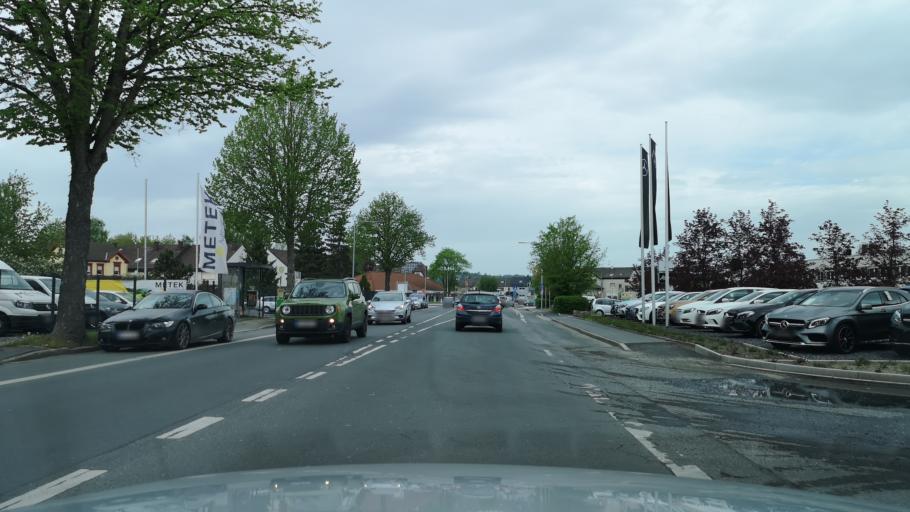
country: DE
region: North Rhine-Westphalia
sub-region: Regierungsbezirk Arnsberg
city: Menden
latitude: 51.4570
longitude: 7.7765
